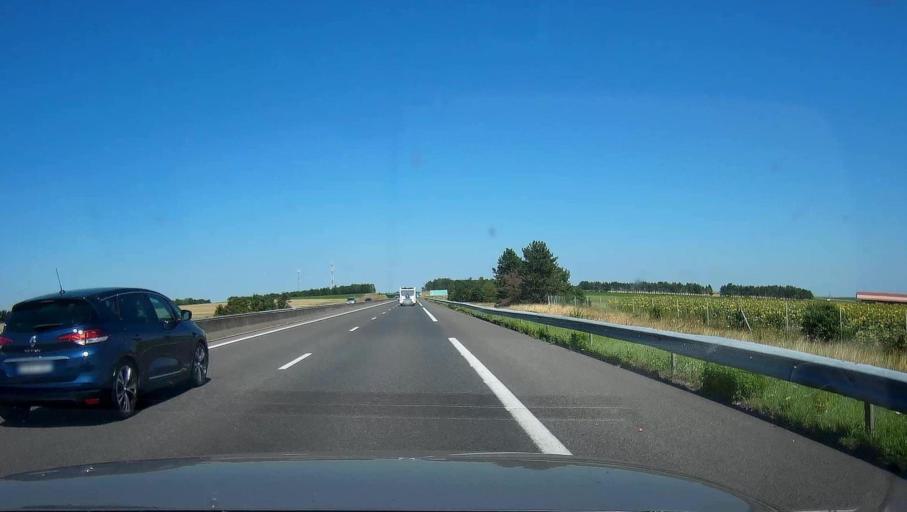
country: FR
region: Champagne-Ardenne
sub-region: Departement de la Marne
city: Compertrix
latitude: 48.8725
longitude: 4.2889
